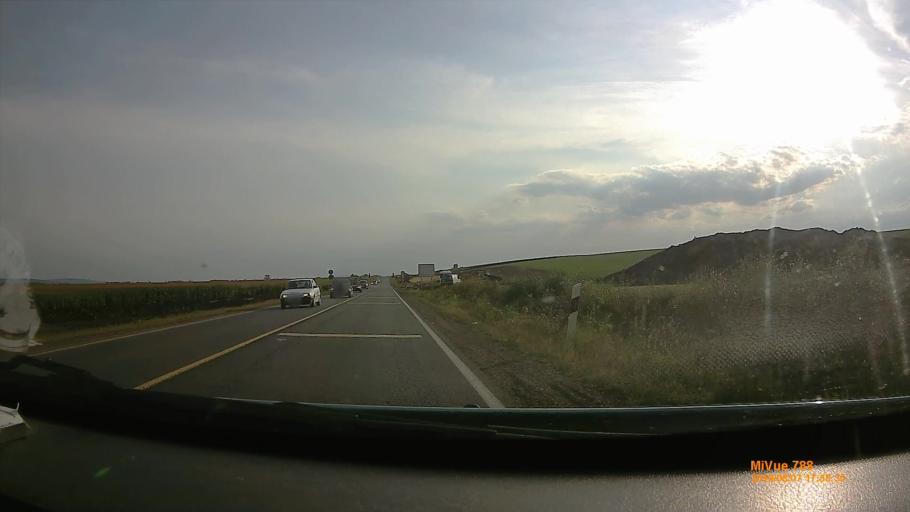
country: HU
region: Borsod-Abauj-Zemplen
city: Encs
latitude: 48.3129
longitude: 21.0782
